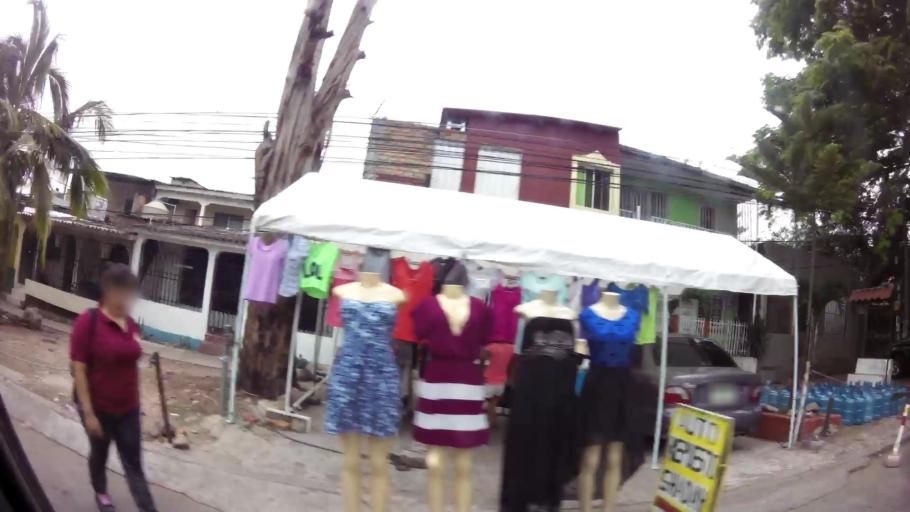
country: HN
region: Francisco Morazan
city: Tegucigalpa
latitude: 14.0751
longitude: -87.1676
